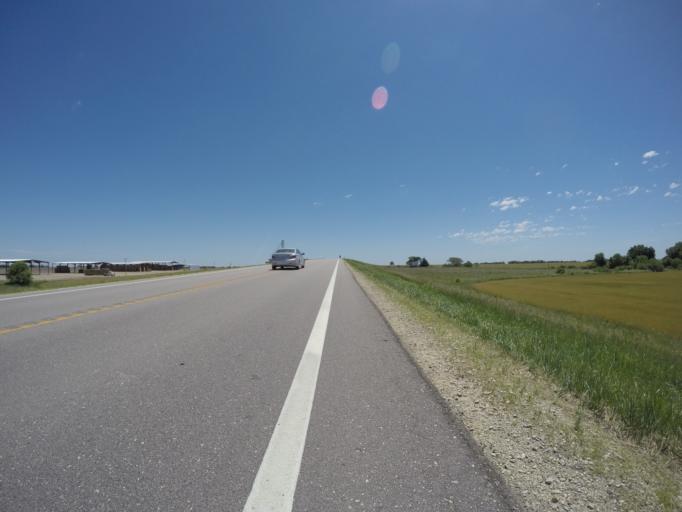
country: US
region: Kansas
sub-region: Republic County
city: Belleville
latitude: 39.8124
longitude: -97.7174
